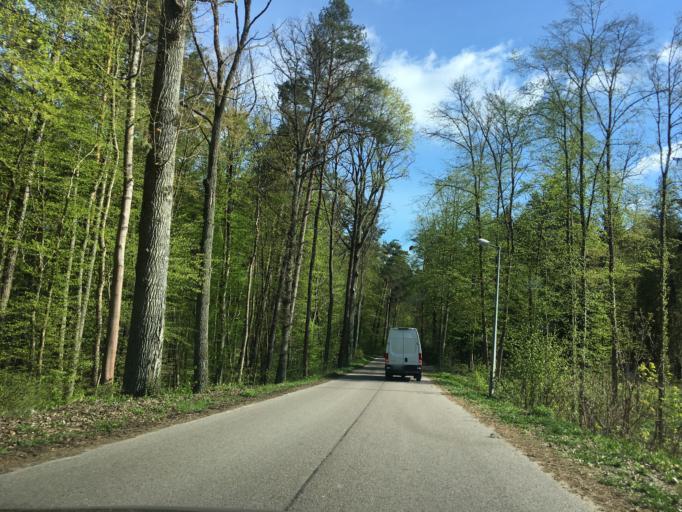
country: PL
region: Warmian-Masurian Voivodeship
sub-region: Powiat piski
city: Ruciane-Nida
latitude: 53.6547
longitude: 21.5573
